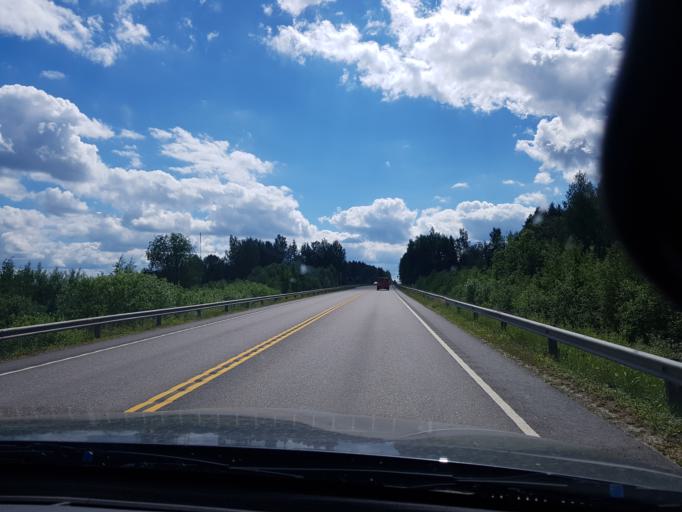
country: FI
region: Haeme
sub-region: Haemeenlinna
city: Parola
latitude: 61.0935
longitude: 24.4031
